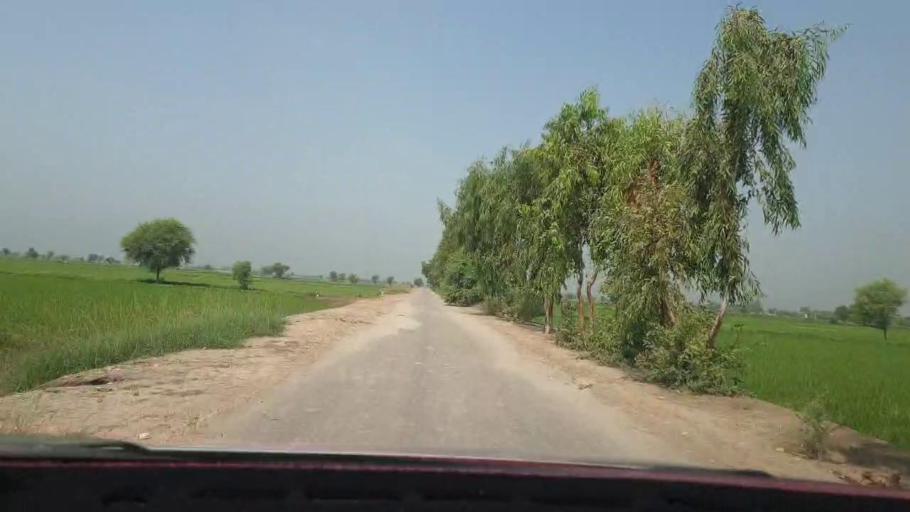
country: PK
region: Sindh
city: Warah
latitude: 27.4304
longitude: 67.8637
